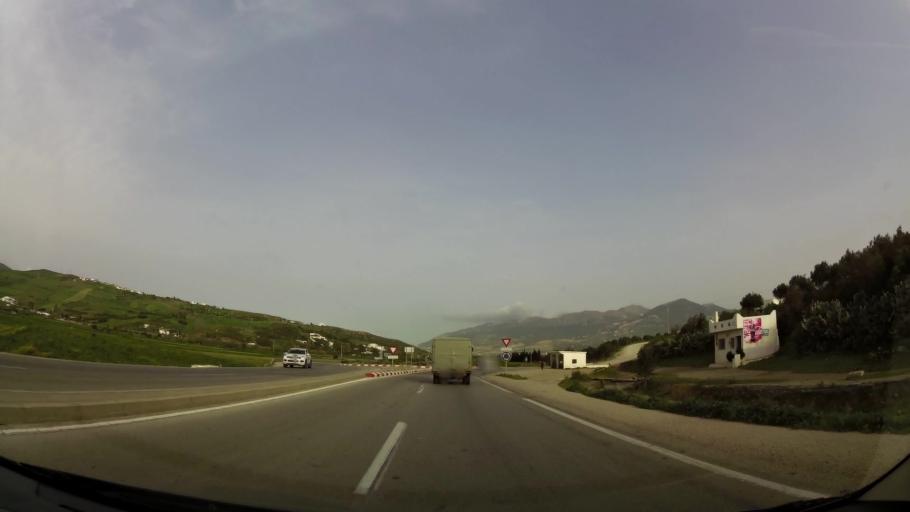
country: MA
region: Tanger-Tetouan
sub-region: Tetouan
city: Saddina
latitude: 35.5603
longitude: -5.4680
